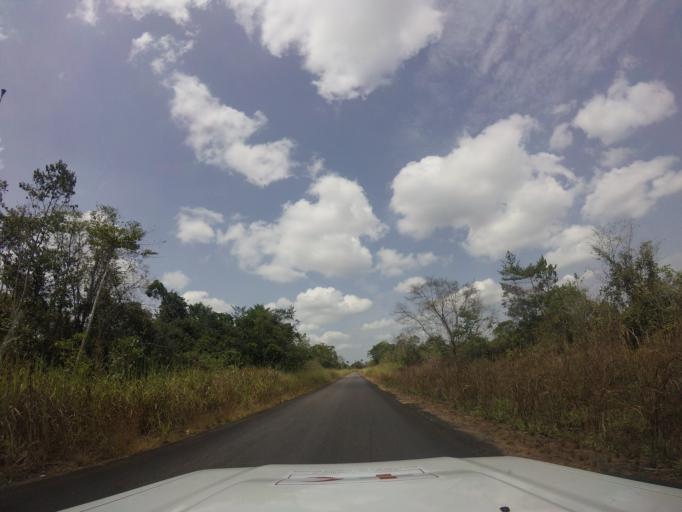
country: LR
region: Grand Cape Mount
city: Robertsport
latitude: 6.9280
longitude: -11.2556
